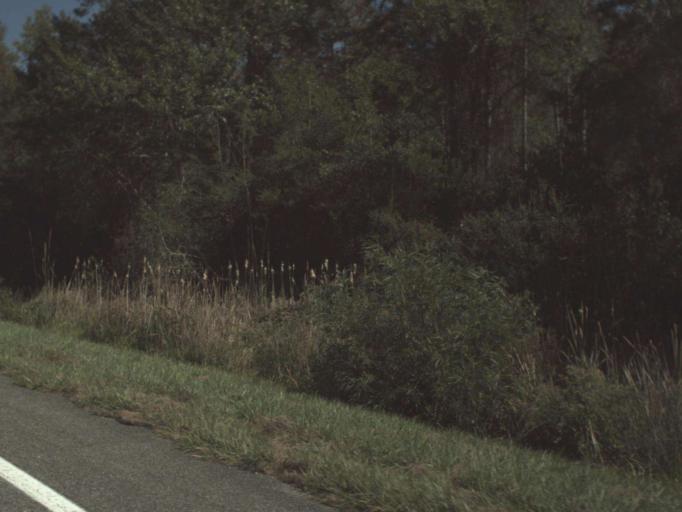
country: US
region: Florida
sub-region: Leon County
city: Woodville
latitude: 30.2014
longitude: -84.0499
